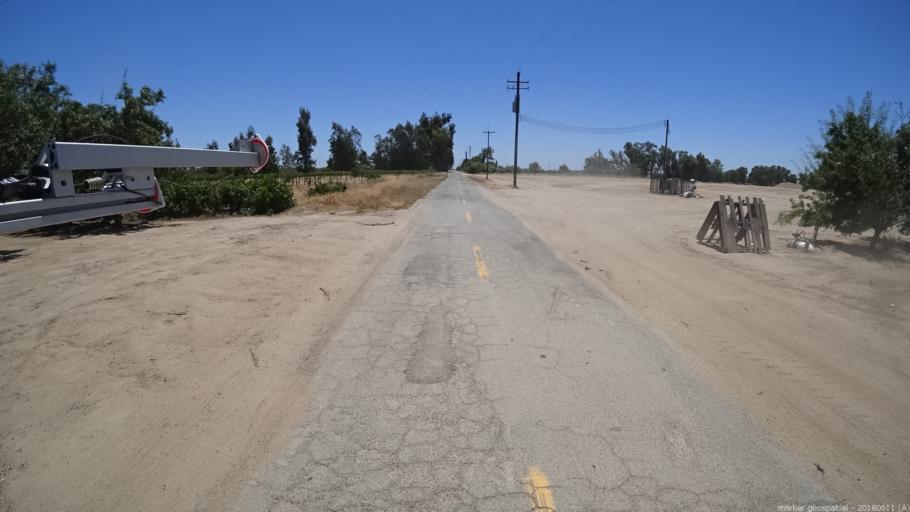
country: US
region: California
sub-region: Madera County
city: Fairmead
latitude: 37.0217
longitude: -120.1933
